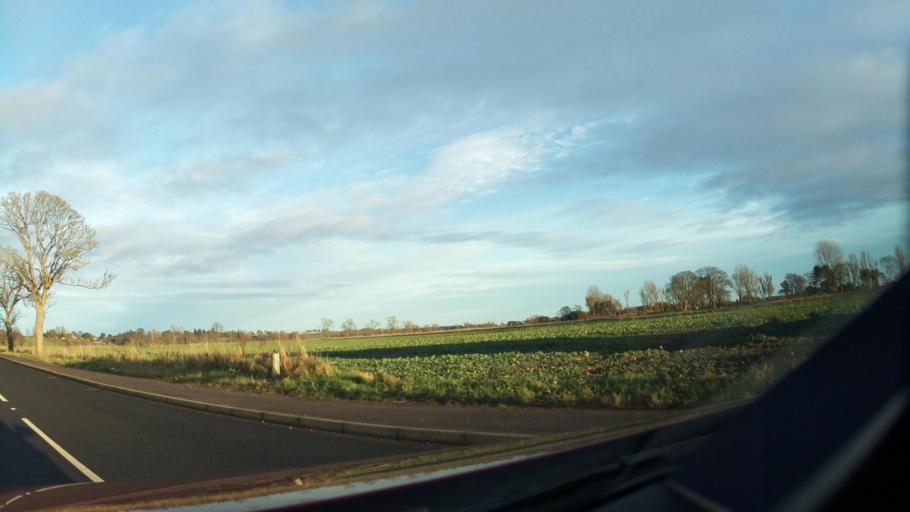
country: GB
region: Scotland
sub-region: Fife
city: Tayport
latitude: 56.4876
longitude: -2.8081
